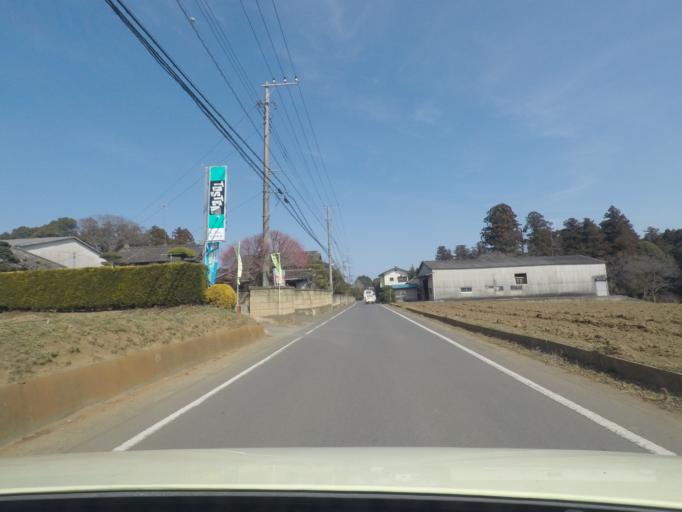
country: JP
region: Ibaraki
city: Okunoya
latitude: 36.2047
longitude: 140.4177
